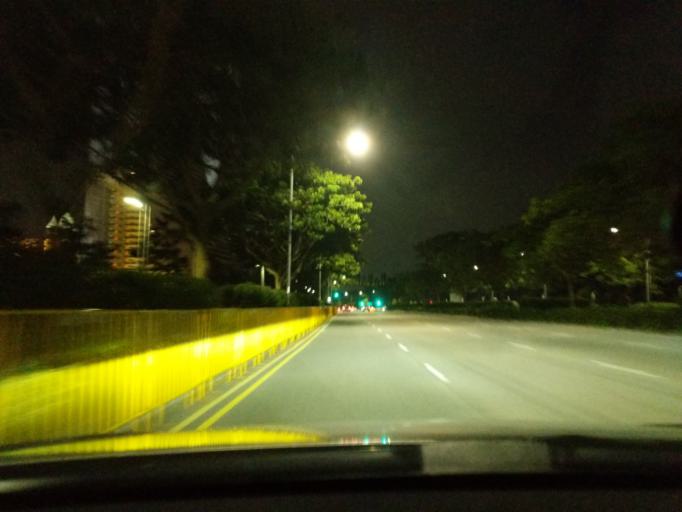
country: SG
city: Singapore
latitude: 1.2801
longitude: 103.8596
